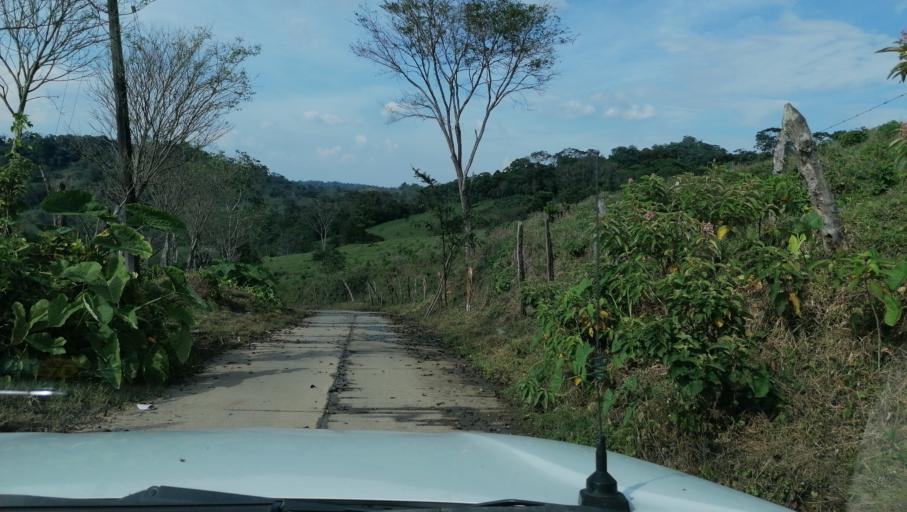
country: MX
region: Chiapas
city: Ostuacan
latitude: 17.4658
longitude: -93.2368
